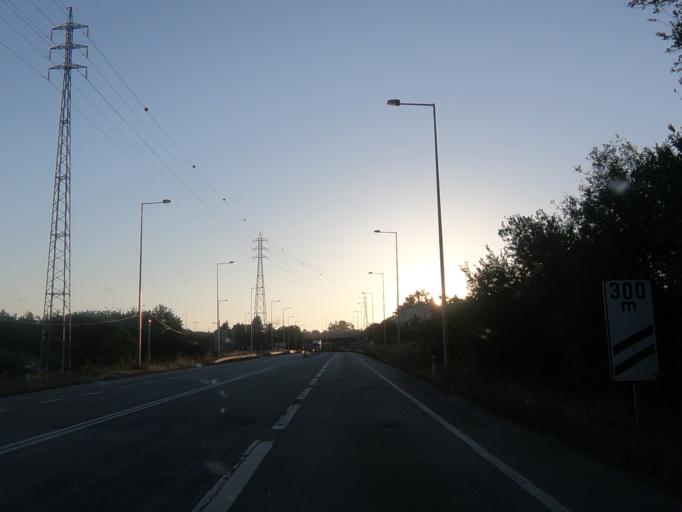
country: PT
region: Viseu
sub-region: Viseu
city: Abraveses
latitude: 40.6917
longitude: -7.9090
